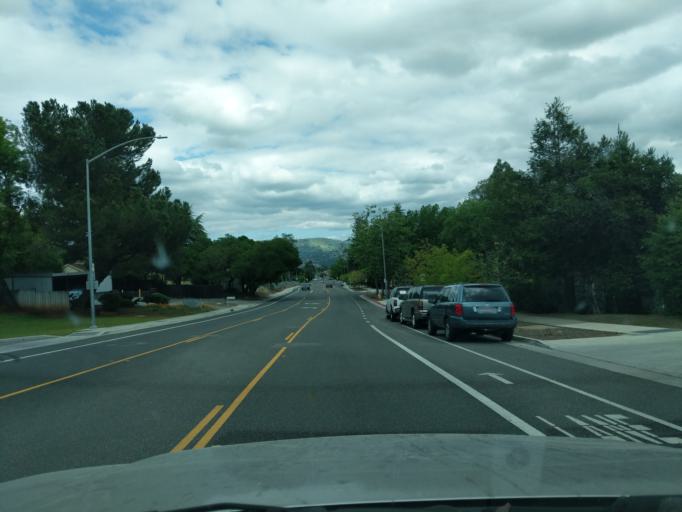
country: US
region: California
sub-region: Santa Clara County
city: Morgan Hill
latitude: 37.1235
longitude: -121.6557
